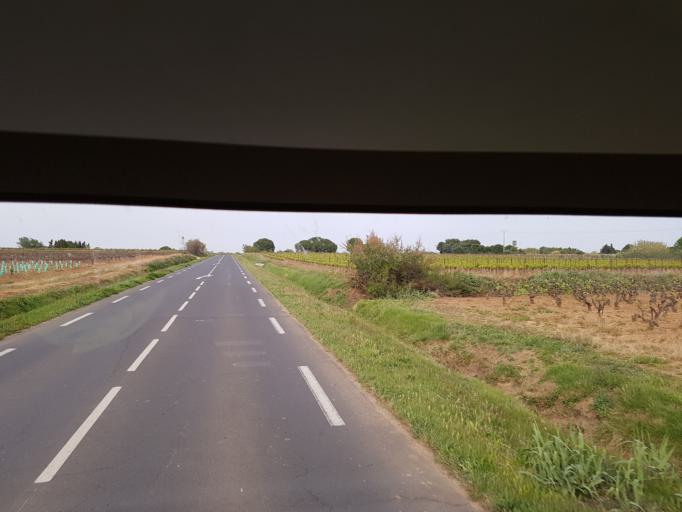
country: FR
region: Languedoc-Roussillon
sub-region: Departement de l'Herault
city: Marseillan
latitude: 43.3484
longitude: 3.5093
